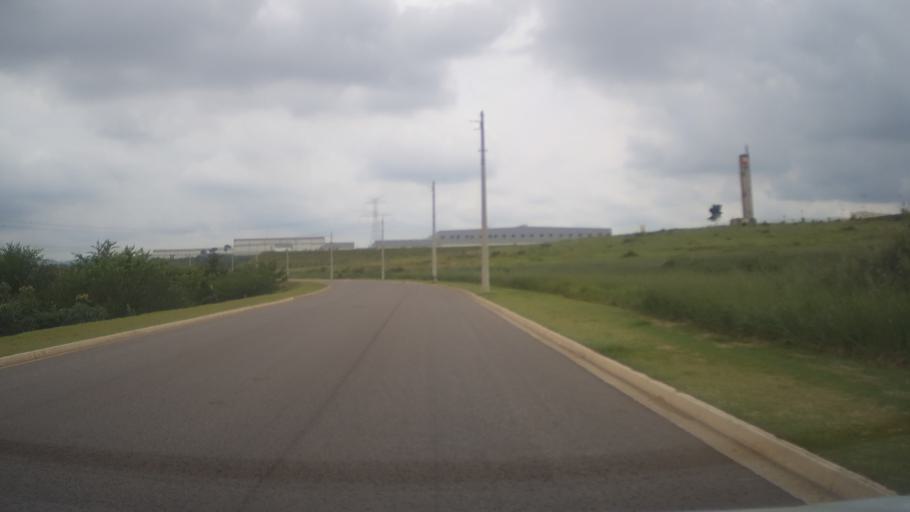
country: BR
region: Sao Paulo
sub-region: Itupeva
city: Itupeva
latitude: -23.1535
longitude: -46.9984
